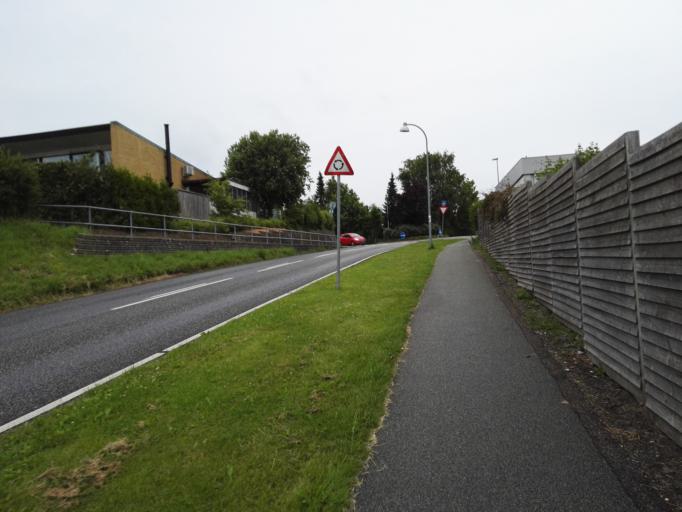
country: DK
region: Capital Region
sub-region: Egedal Kommune
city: Smorumnedre
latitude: 55.7431
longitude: 12.2951
